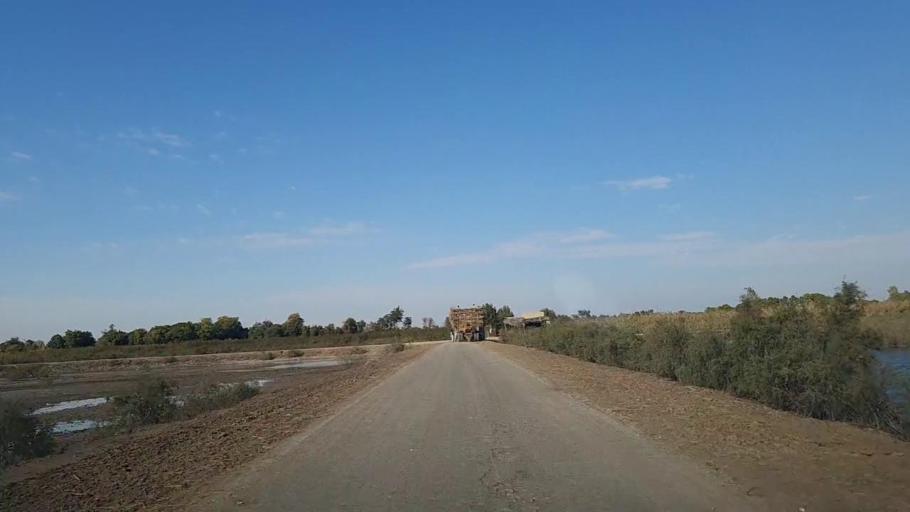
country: PK
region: Sindh
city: Khadro
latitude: 26.3012
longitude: 68.8202
